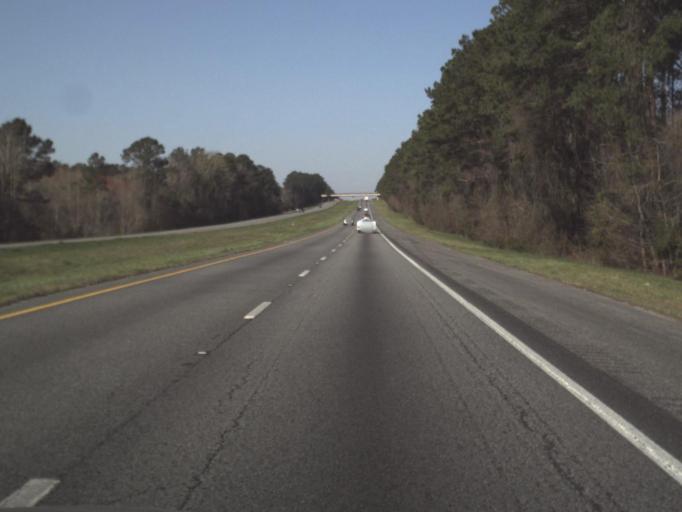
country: US
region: Florida
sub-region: Jefferson County
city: Monticello
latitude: 30.4884
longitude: -83.9717
